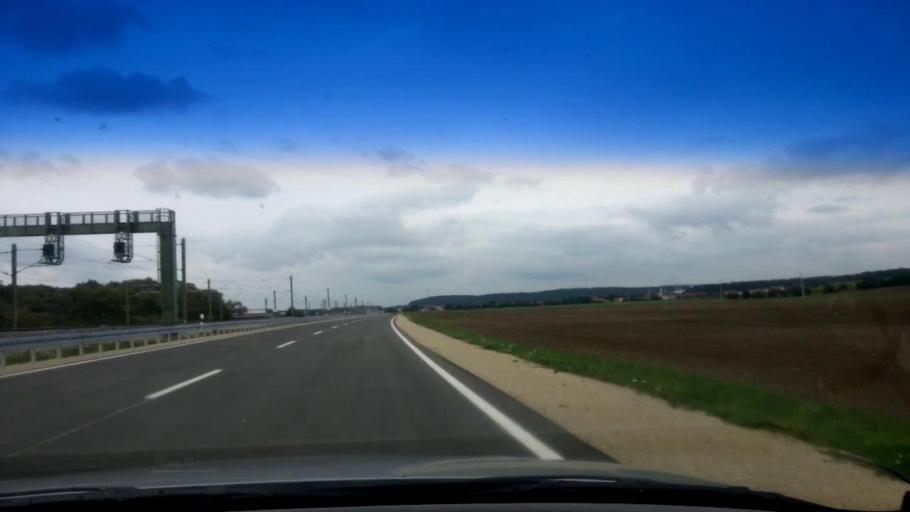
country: DE
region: Bavaria
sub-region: Upper Franconia
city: Zapfendorf
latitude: 50.0075
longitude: 10.9192
